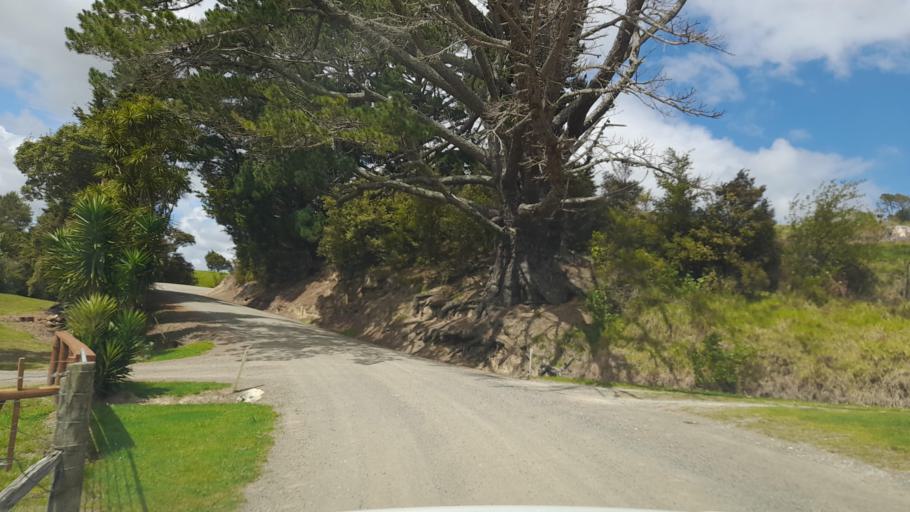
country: NZ
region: Auckland
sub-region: Auckland
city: Wellsford
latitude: -36.1990
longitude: 174.3372
